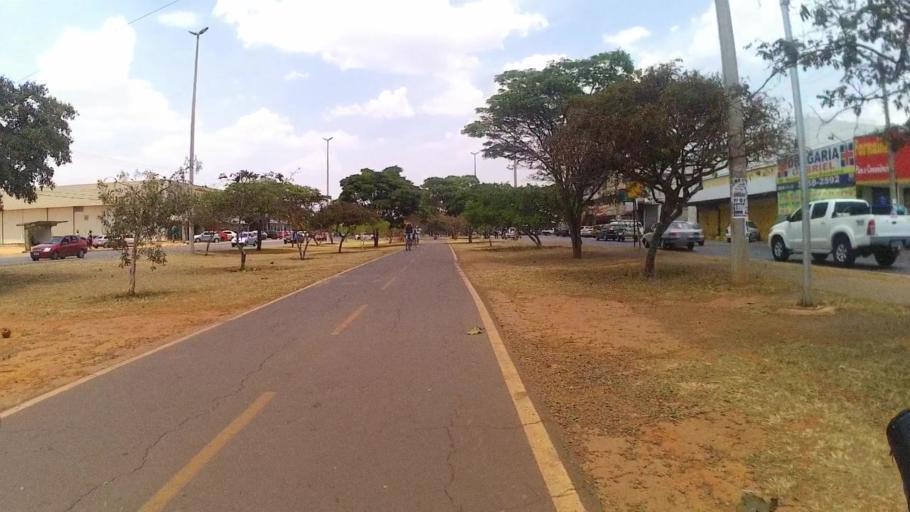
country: BR
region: Federal District
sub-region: Brasilia
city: Brasilia
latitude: -15.8702
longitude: -48.0617
